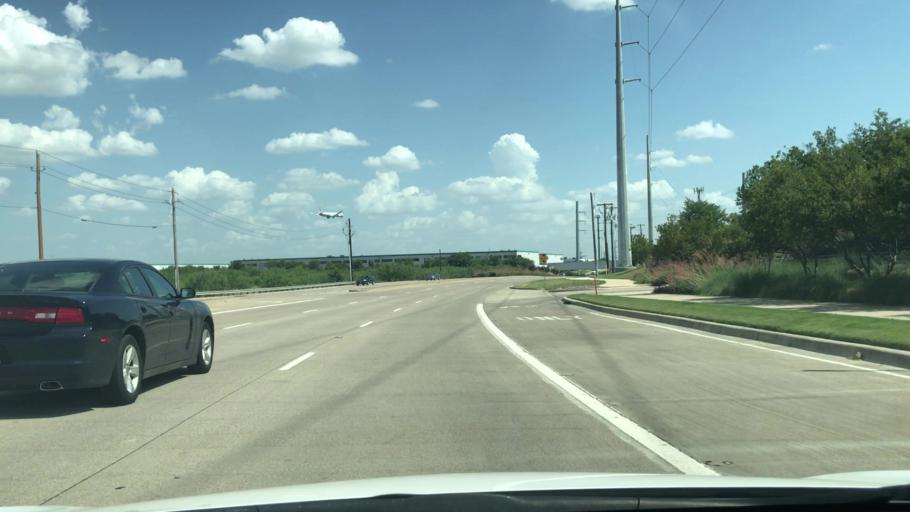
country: US
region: Texas
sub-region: Tarrant County
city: Grapevine
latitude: 32.9389
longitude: -97.0635
